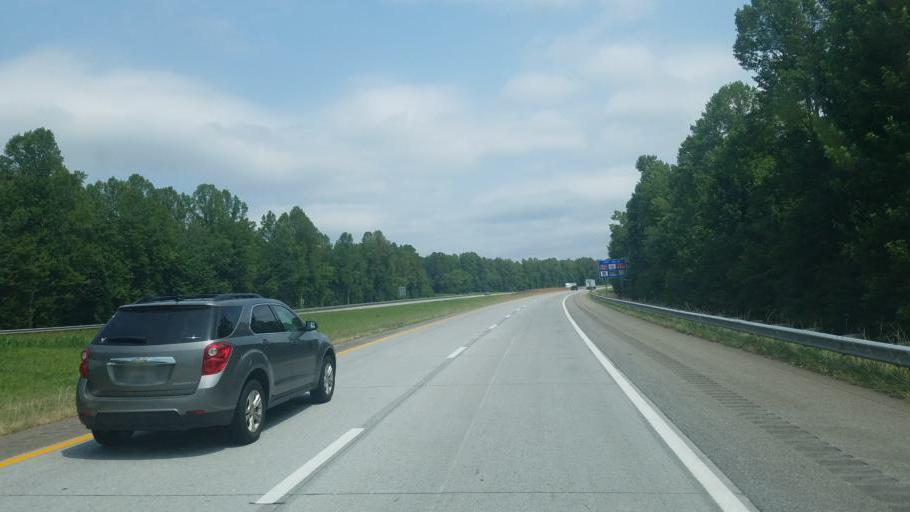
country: US
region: North Carolina
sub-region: Surry County
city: Elkin
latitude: 36.2703
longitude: -80.8253
